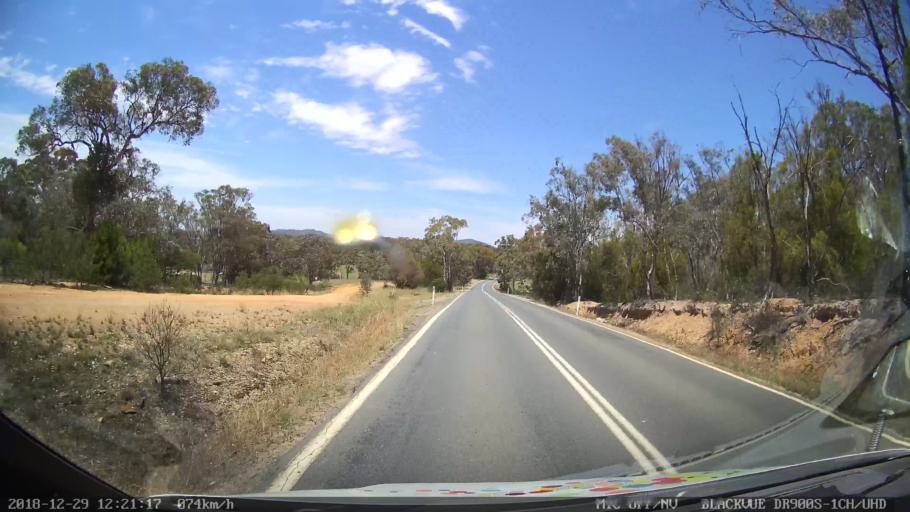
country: AU
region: New South Wales
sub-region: Queanbeyan
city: Queanbeyan
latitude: -35.4118
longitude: 149.2245
